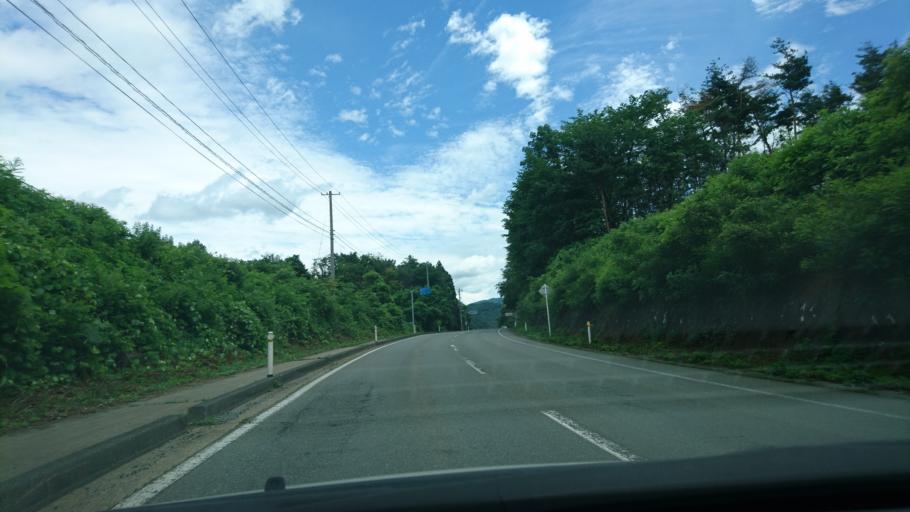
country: JP
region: Iwate
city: Morioka-shi
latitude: 39.6006
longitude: 141.2030
